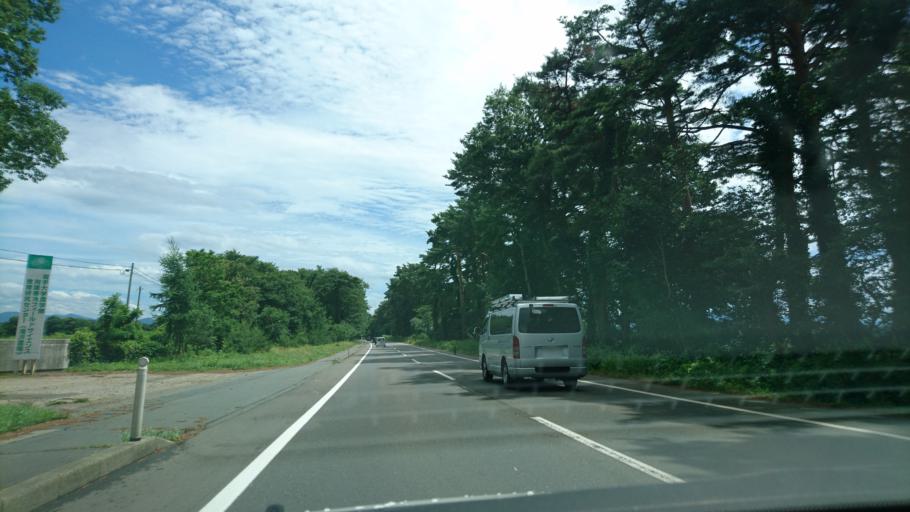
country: JP
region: Iwate
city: Morioka-shi
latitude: 39.7801
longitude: 141.1260
